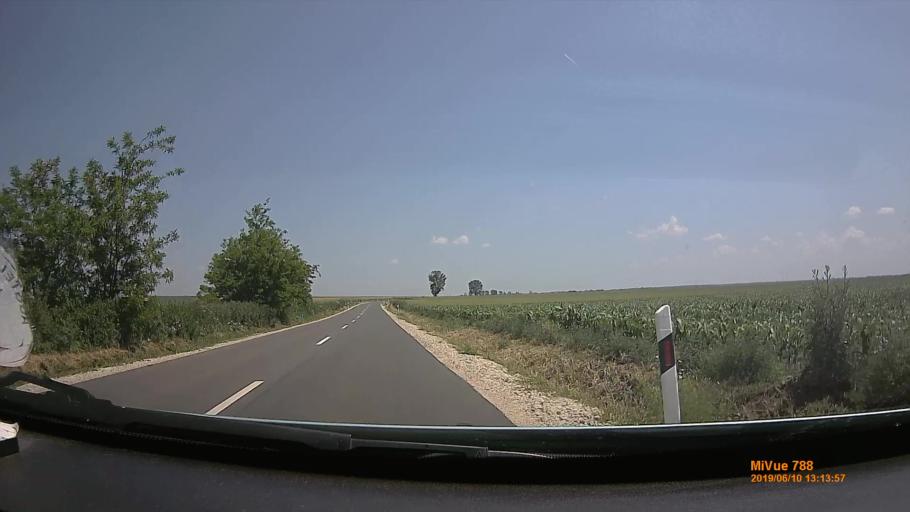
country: HU
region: Borsod-Abauj-Zemplen
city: Hernadnemeti
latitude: 48.0586
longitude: 21.0137
